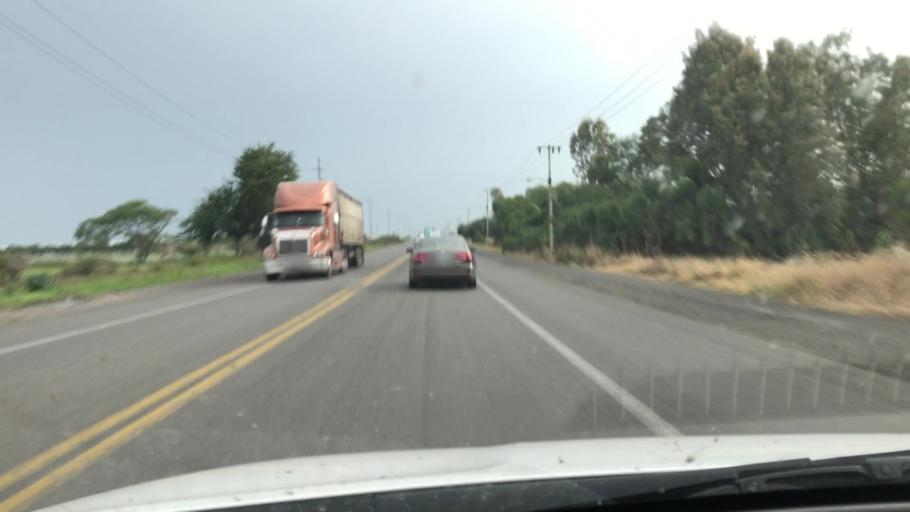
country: MX
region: Michoacan
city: Tanhuato de Guerrero
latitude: 20.2788
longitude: -102.3720
